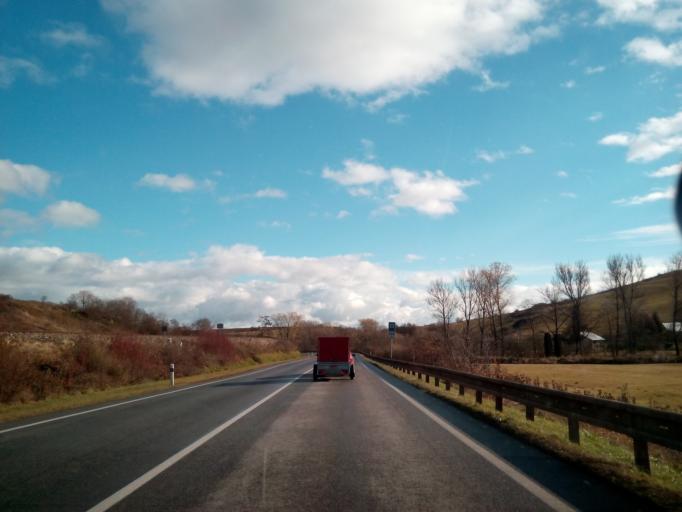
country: SK
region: Presovsky
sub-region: Okres Bardejov
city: Bardejov
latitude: 49.1387
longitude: 21.3196
